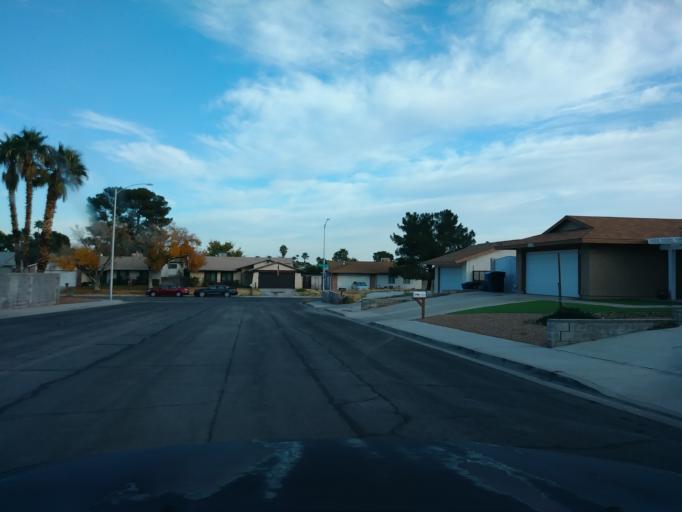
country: US
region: Nevada
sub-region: Clark County
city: Spring Valley
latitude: 36.1672
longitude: -115.2411
